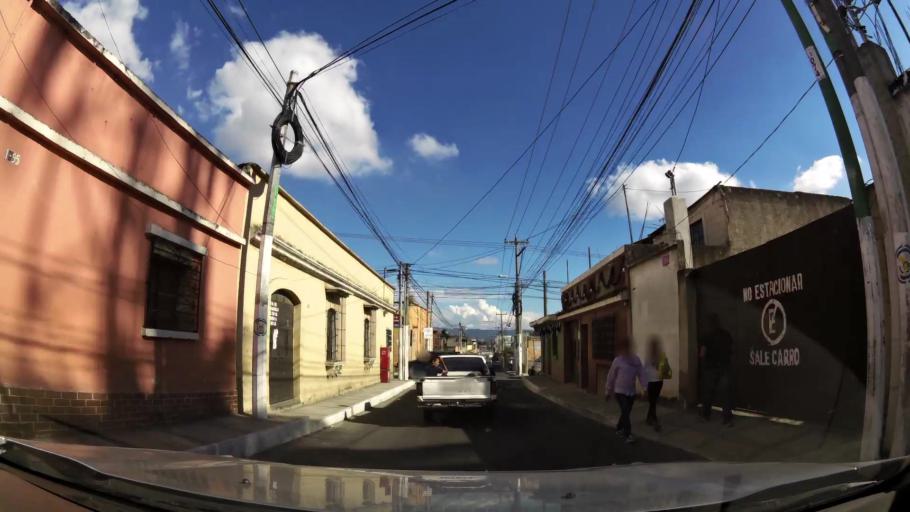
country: GT
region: Guatemala
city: Villa Nueva
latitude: 14.5259
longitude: -90.5915
